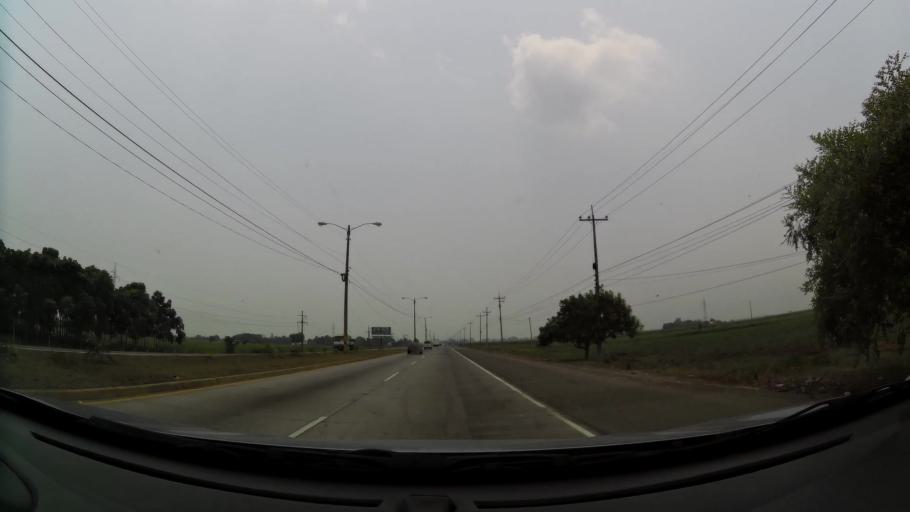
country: HN
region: Cortes
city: La Lima
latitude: 15.4116
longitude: -87.8695
